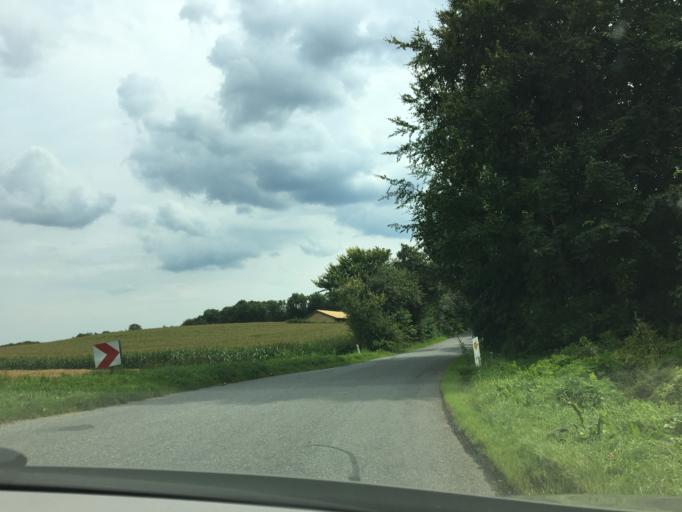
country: DK
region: Central Jutland
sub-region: Viborg Kommune
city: Stoholm
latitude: 56.4613
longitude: 9.1617
